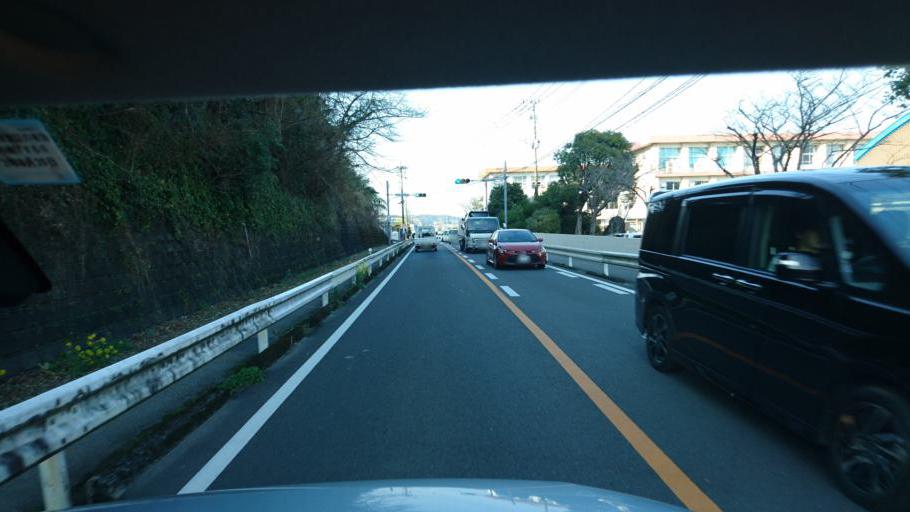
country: JP
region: Miyazaki
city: Miyazaki-shi
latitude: 31.9838
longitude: 131.4400
